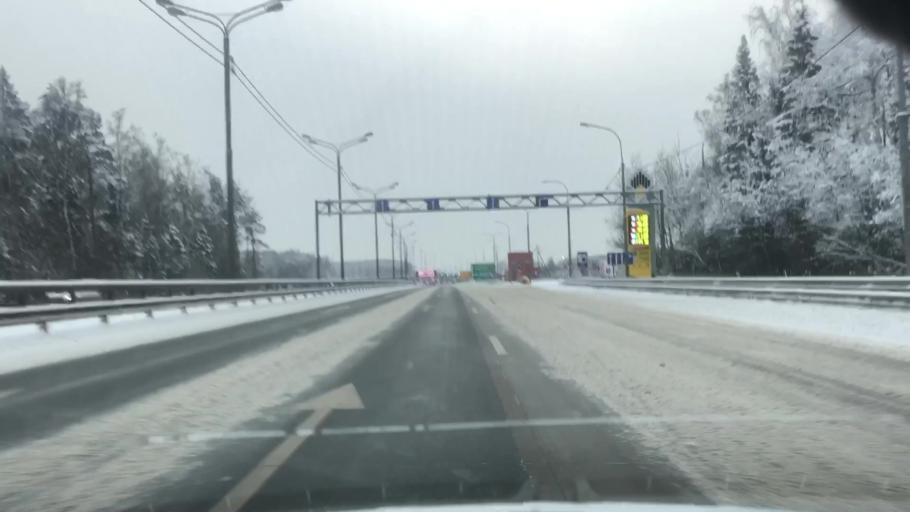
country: RU
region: Moskovskaya
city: Mikhnevo
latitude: 55.1743
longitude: 37.9118
